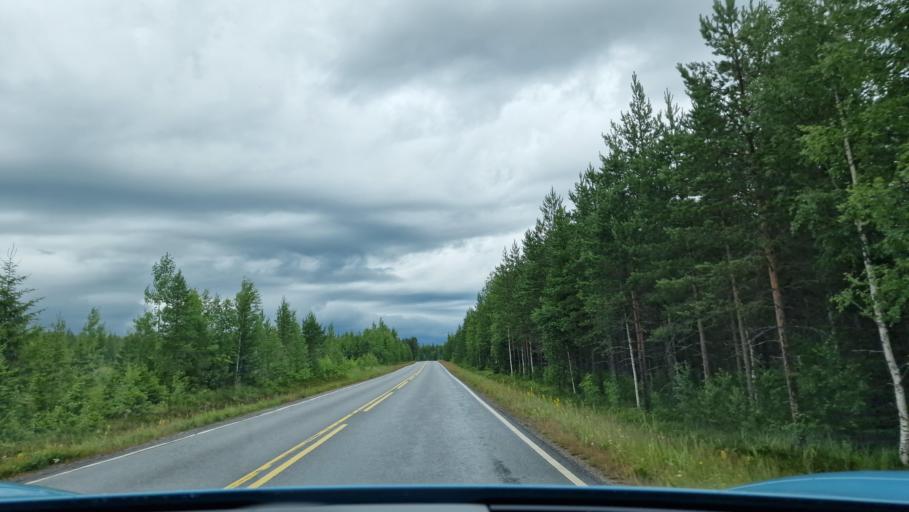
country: FI
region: Southern Ostrobothnia
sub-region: Jaerviseutu
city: Soini
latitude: 62.7124
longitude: 24.4402
